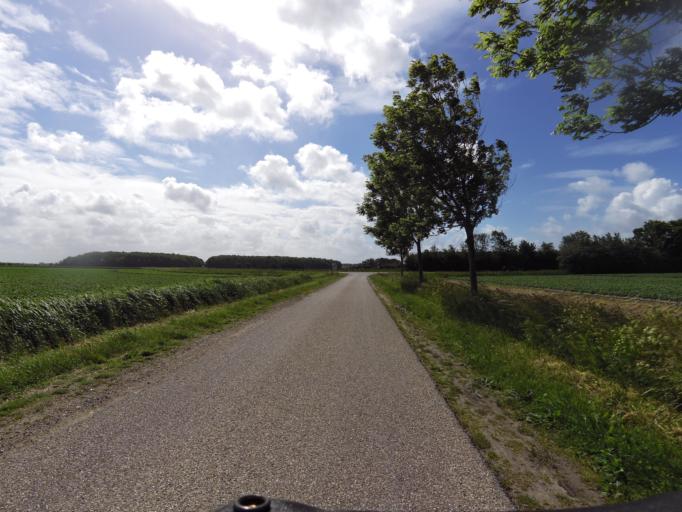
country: NL
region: Zeeland
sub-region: Schouwen-Duiveland
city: Bruinisse
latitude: 51.6847
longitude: 4.0045
